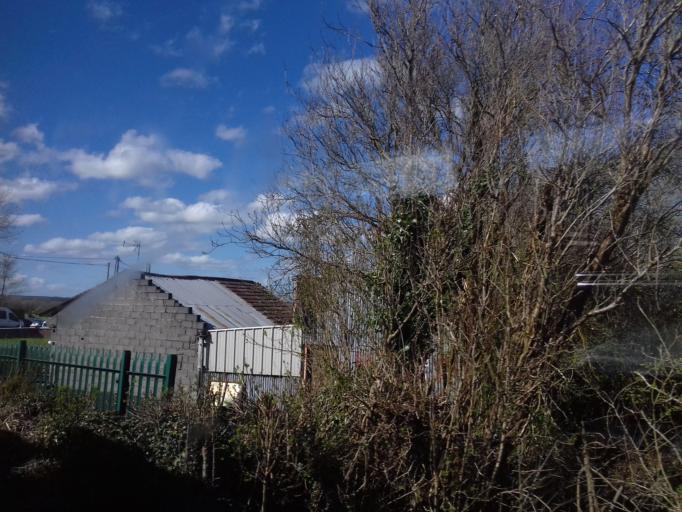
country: IE
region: Munster
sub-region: County Cork
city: Kanturk
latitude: 52.1269
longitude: -8.8220
